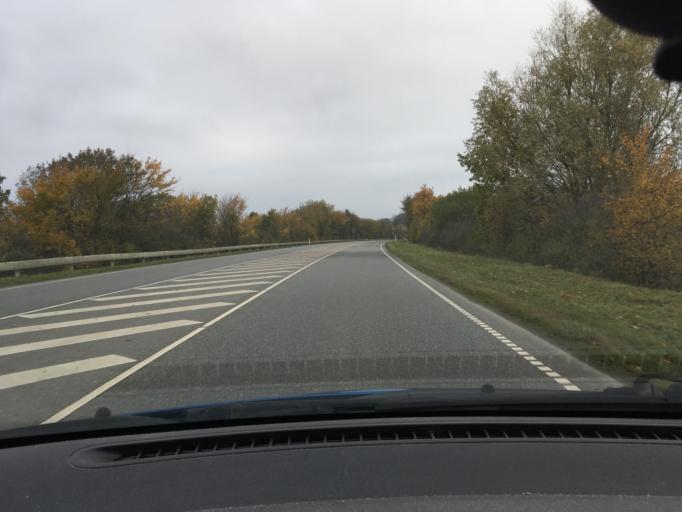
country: DK
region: South Denmark
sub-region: Aabenraa Kommune
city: Aabenraa
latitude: 55.0082
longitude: 9.4199
